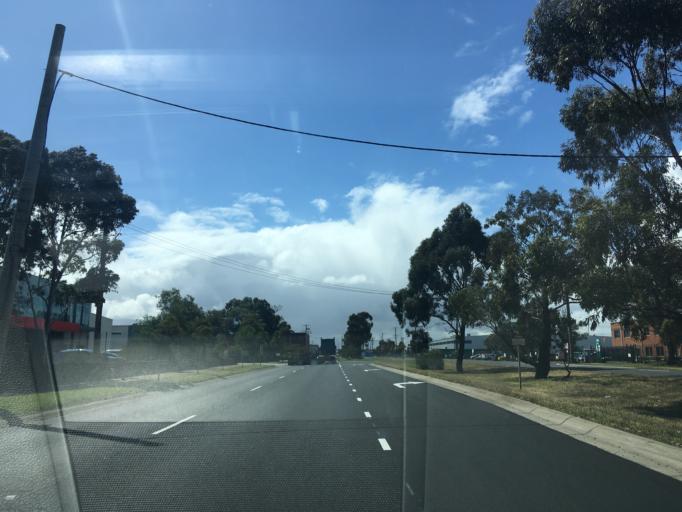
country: AU
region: Victoria
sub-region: Brimbank
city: Derrimut
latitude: -37.8179
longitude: 144.7867
